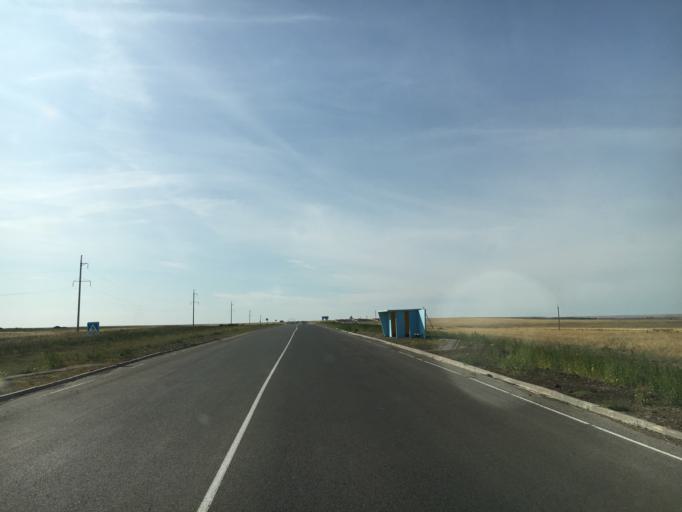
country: KZ
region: Batys Qazaqstan
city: Kamenka
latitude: 51.1187
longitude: 50.1946
